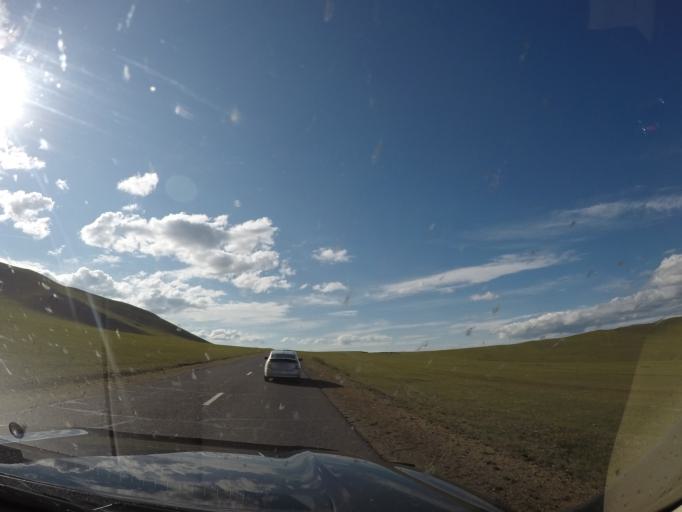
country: MN
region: Hentiy
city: Modot
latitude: 47.7496
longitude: 108.9642
